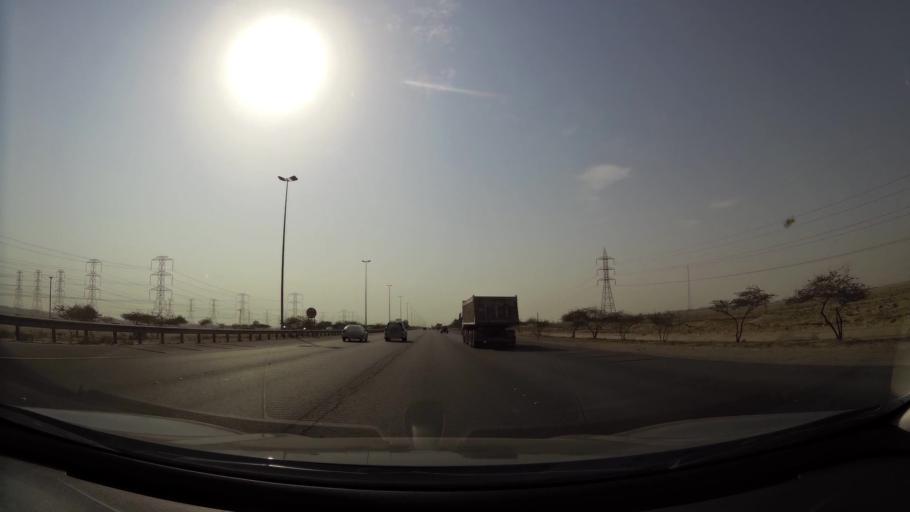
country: KW
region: Al Ahmadi
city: Al Ahmadi
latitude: 28.9830
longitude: 48.1064
